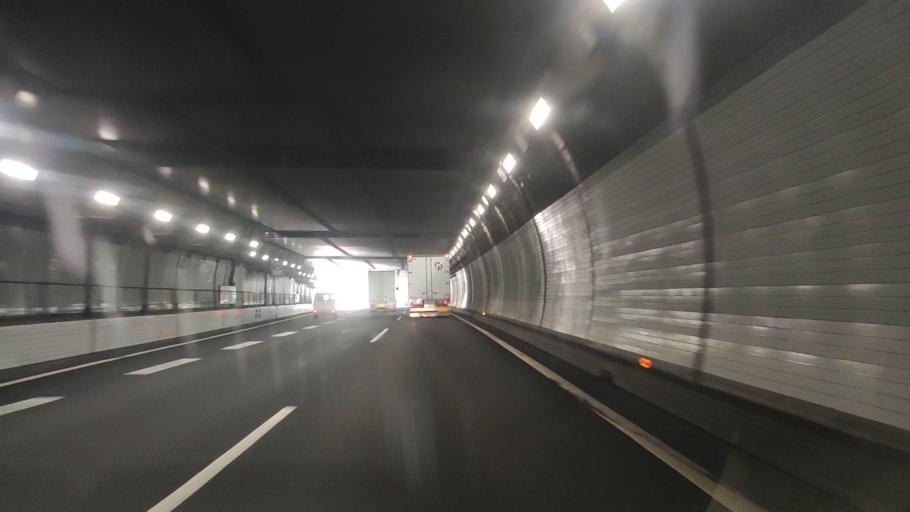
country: JP
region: Tokyo
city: Hachioji
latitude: 35.6447
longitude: 139.2530
